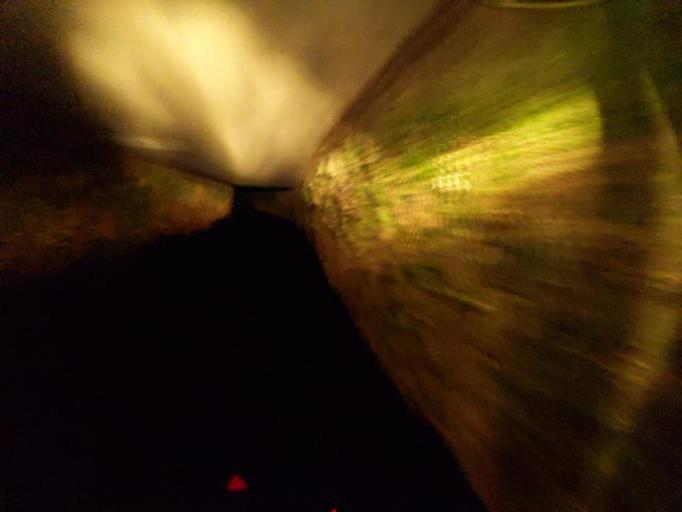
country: GB
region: England
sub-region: Cornwall
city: Torpoint
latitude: 50.3476
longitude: -4.2262
